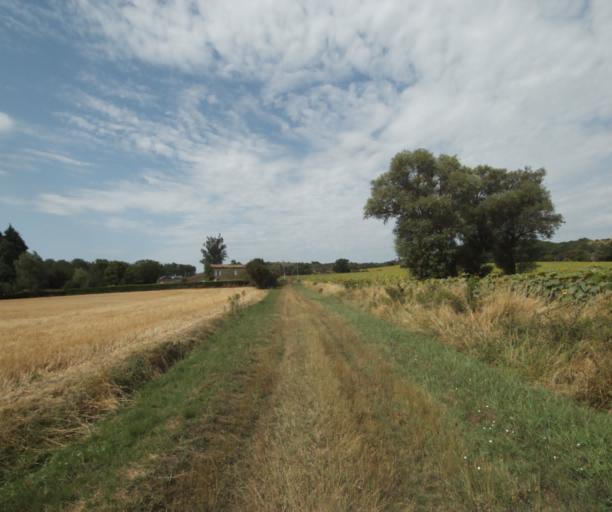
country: FR
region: Midi-Pyrenees
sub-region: Departement de la Haute-Garonne
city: Saint-Felix-Lauragais
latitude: 43.4521
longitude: 1.9135
